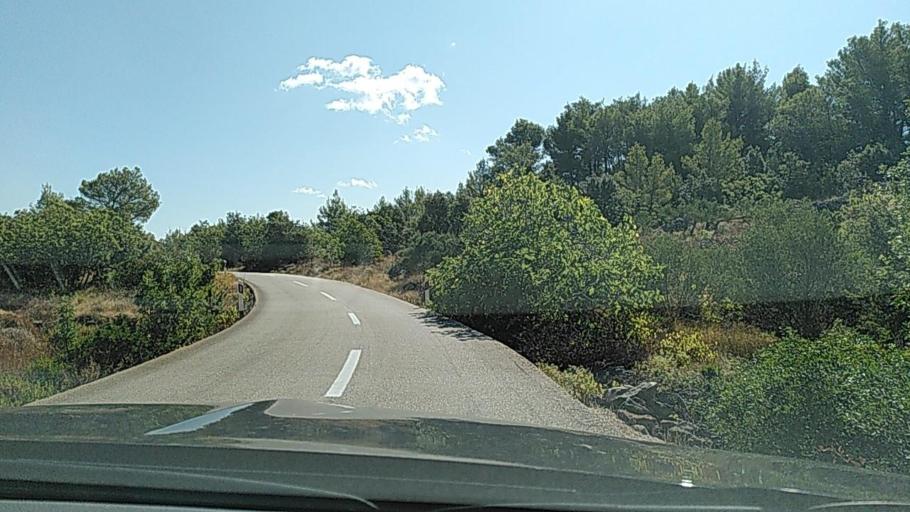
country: HR
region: Splitsko-Dalmatinska
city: Jelsa
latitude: 43.1445
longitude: 16.8033
